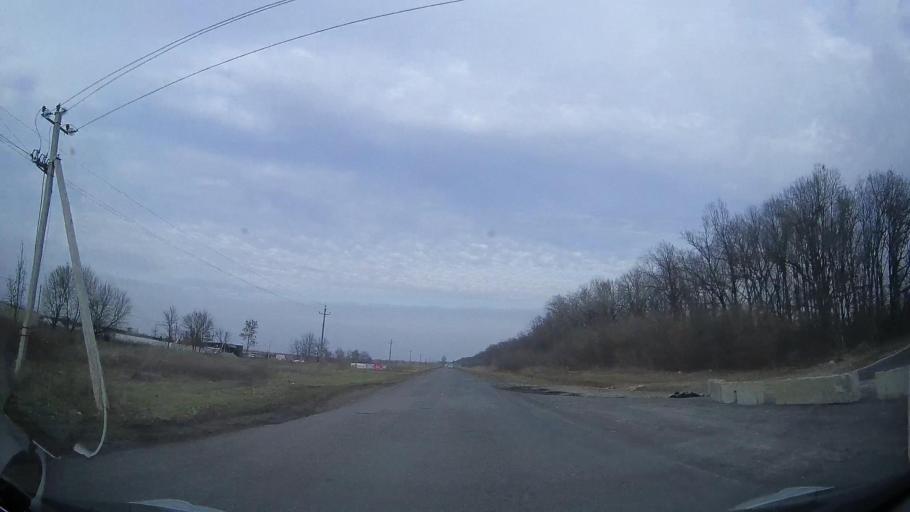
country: RU
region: Rostov
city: Ol'ginskaya
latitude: 47.1366
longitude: 39.8944
